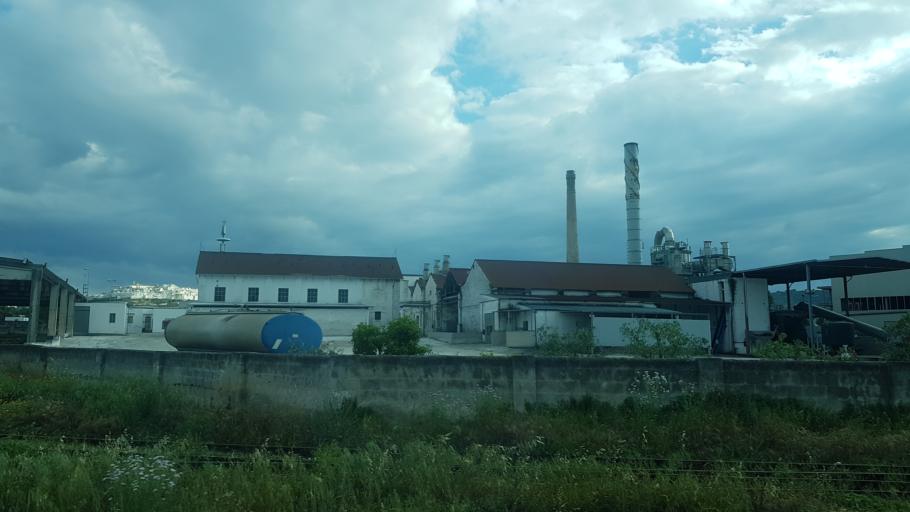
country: IT
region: Apulia
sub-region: Provincia di Brindisi
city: Ostuni
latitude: 40.7530
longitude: 17.5782
